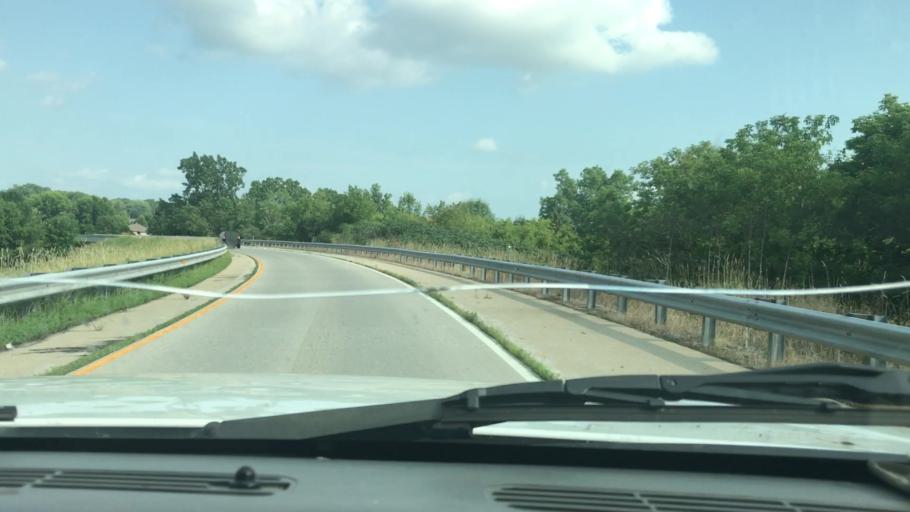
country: US
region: Wisconsin
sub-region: Brown County
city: Green Bay
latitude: 44.5173
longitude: -87.9594
